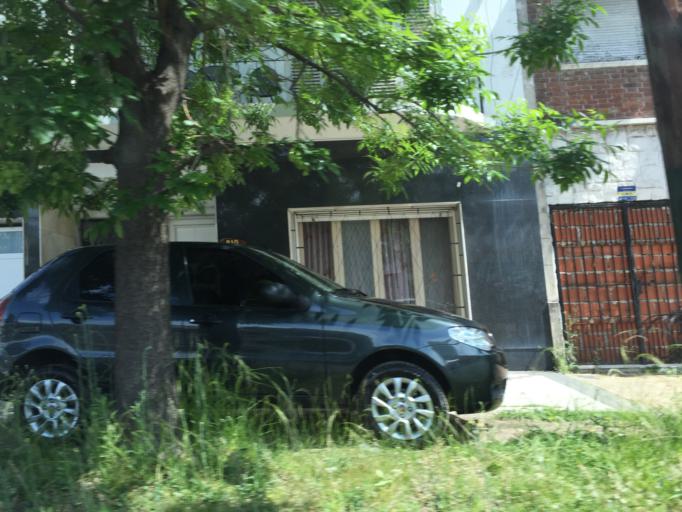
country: AR
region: Buenos Aires
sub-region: Partido de Lomas de Zamora
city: Lomas de Zamora
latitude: -34.7536
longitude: -58.4076
